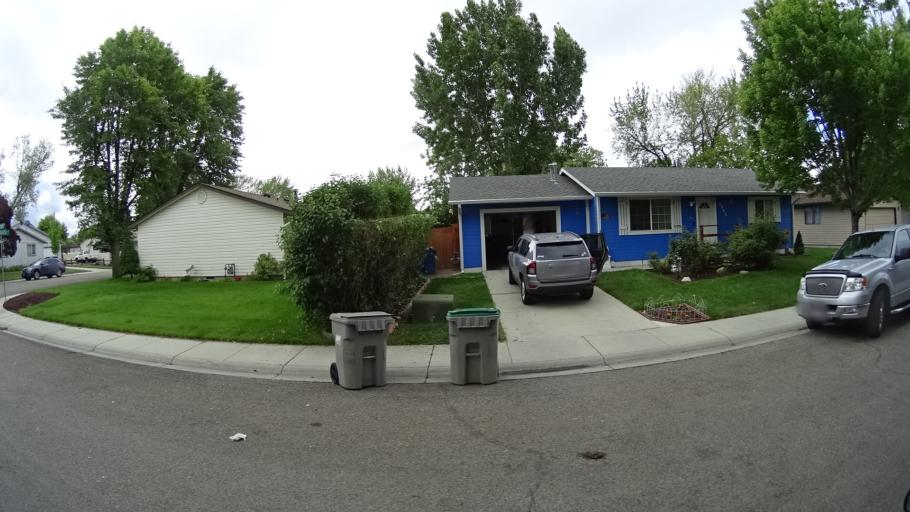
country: US
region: Idaho
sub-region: Ada County
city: Garden City
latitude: 43.6725
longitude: -116.2748
